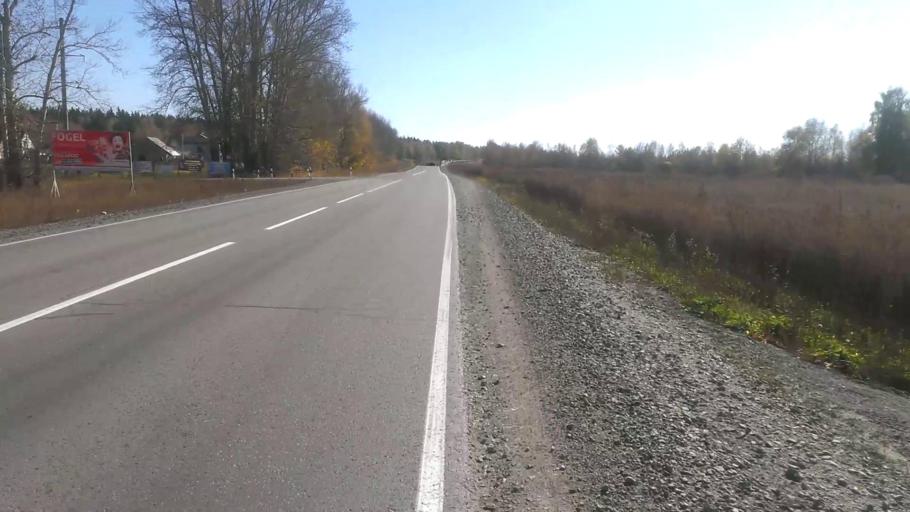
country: RU
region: Altai Krai
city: Sannikovo
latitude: 53.3076
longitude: 83.9679
